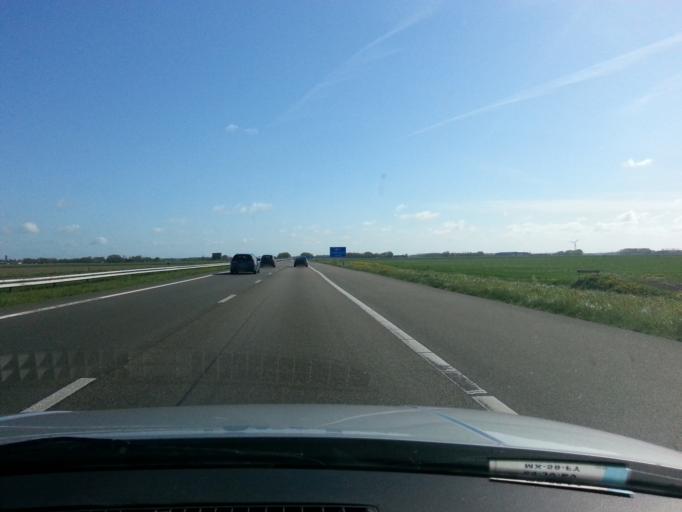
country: NL
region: Flevoland
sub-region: Gemeente Noordoostpolder
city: Emmeloord
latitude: 52.6727
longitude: 5.7174
